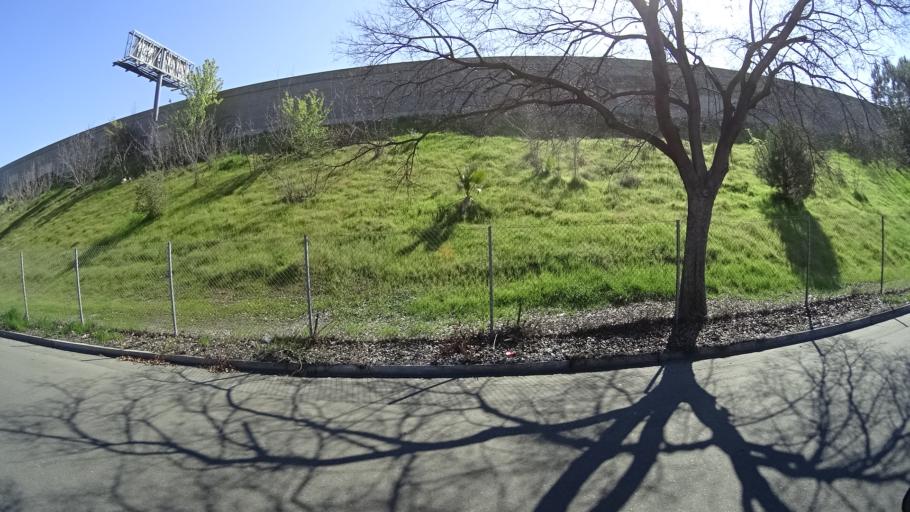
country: US
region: California
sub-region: Fresno County
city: Tarpey Village
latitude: 36.8027
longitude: -119.7395
